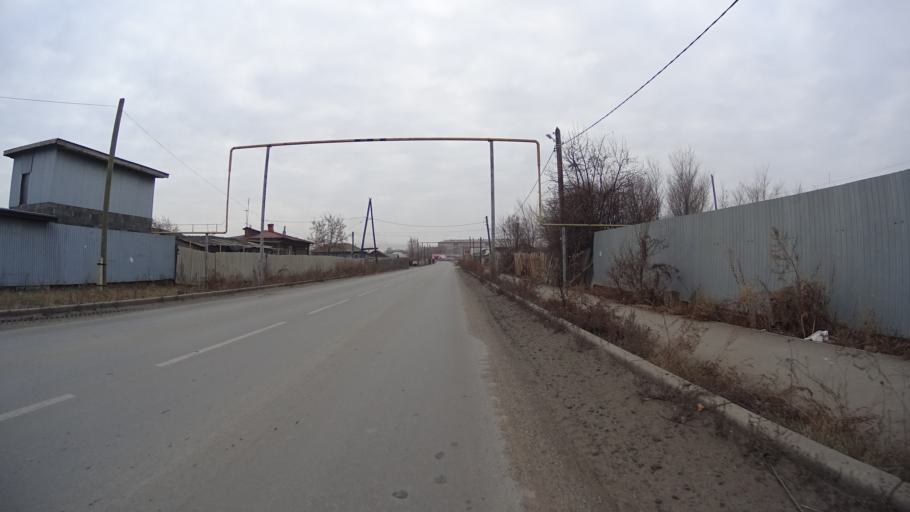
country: RU
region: Chelyabinsk
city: Troitsk
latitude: 54.1058
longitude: 61.5660
